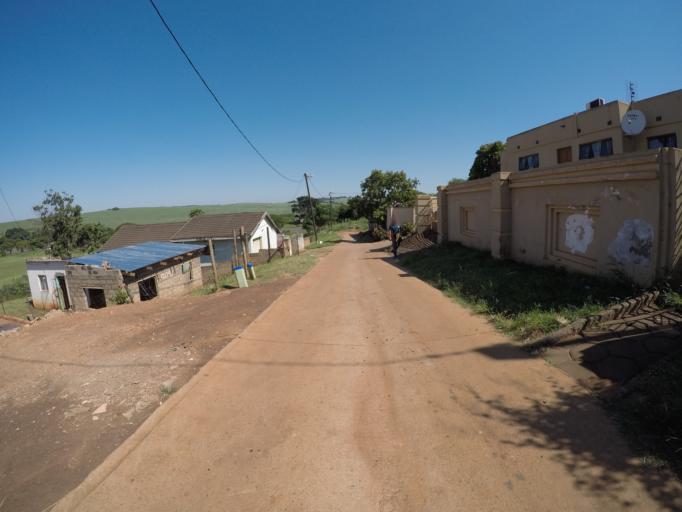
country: ZA
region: KwaZulu-Natal
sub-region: uThungulu District Municipality
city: Empangeni
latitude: -28.7773
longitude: 31.8790
